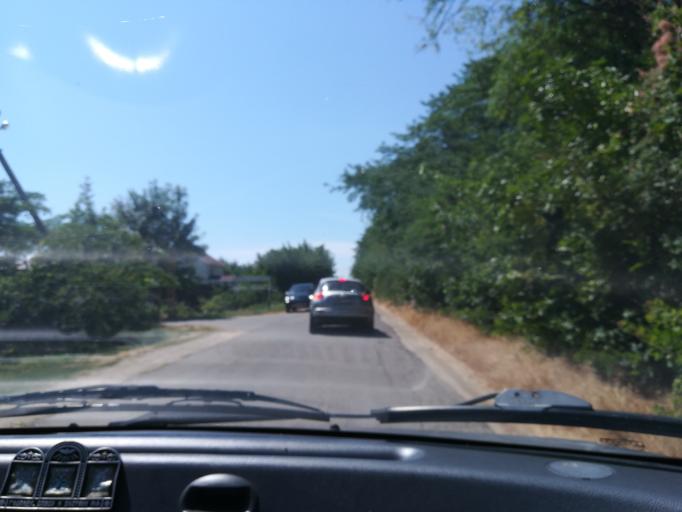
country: RU
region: Krasnodarskiy
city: Blagovetschenskaya
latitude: 45.0554
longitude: 37.1157
